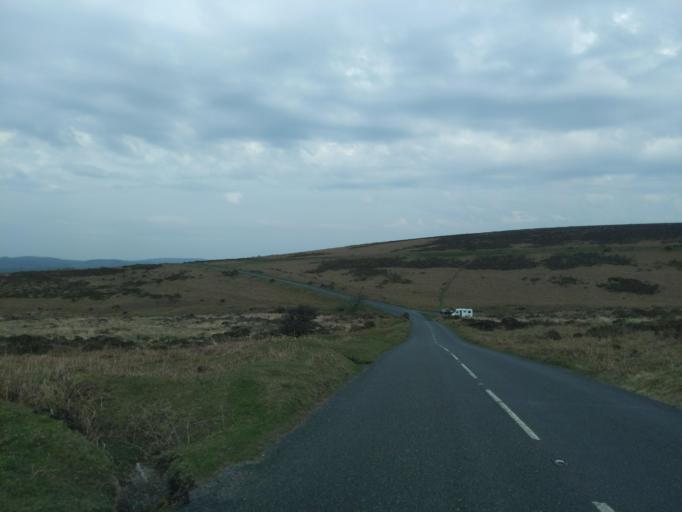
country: GB
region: England
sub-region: Devon
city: Ashburton
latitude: 50.6309
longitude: -3.8517
